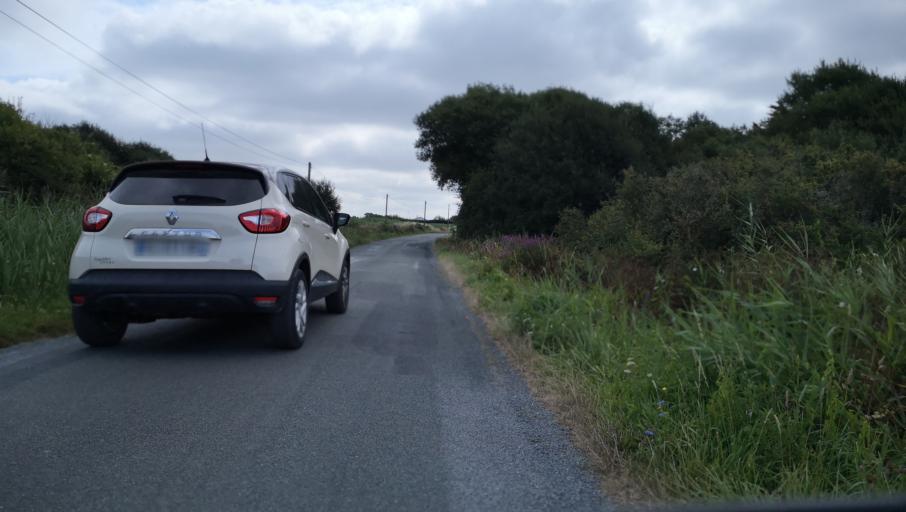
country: FR
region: Pays de la Loire
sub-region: Departement de la Vendee
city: Bretignolles-sur-Mer
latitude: 46.5965
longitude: -1.8224
